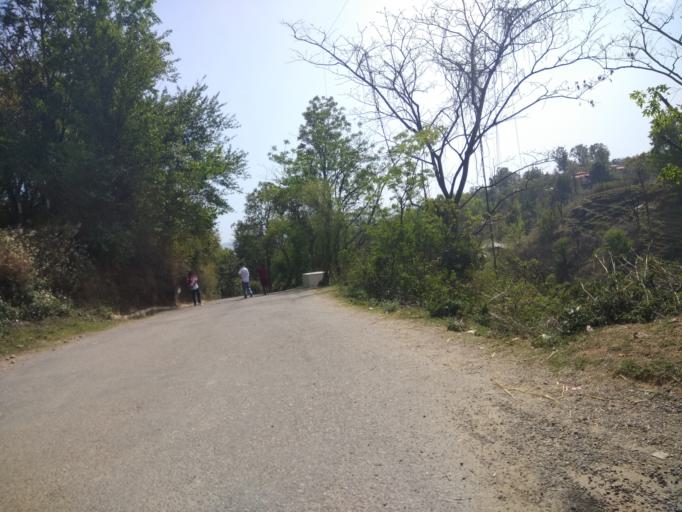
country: IN
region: Himachal Pradesh
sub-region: Kangra
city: Palampur
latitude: 32.0668
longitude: 76.6233
